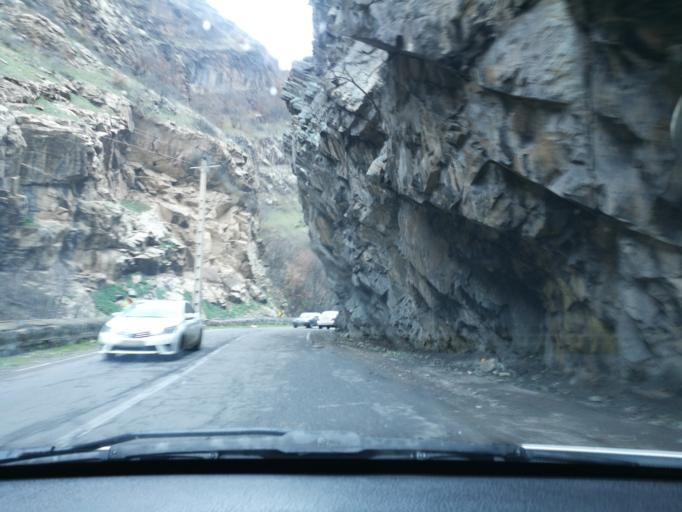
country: IR
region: Mazandaran
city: Chalus
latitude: 36.2965
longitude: 51.2463
